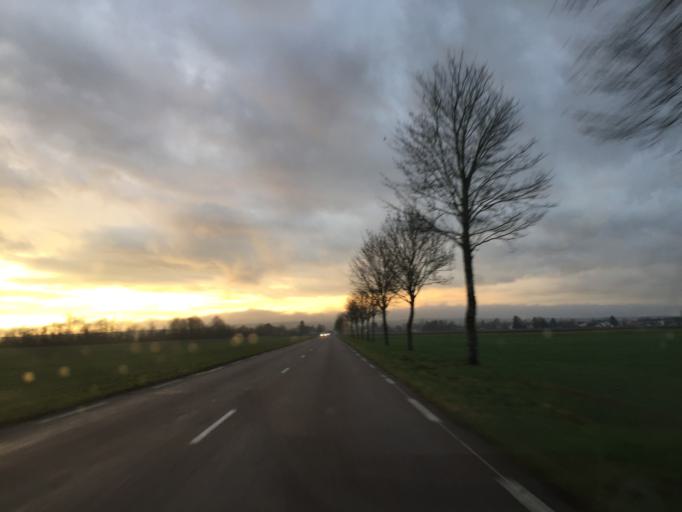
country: FR
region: Franche-Comte
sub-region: Departement du Jura
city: Choisey
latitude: 47.0342
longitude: 5.4953
